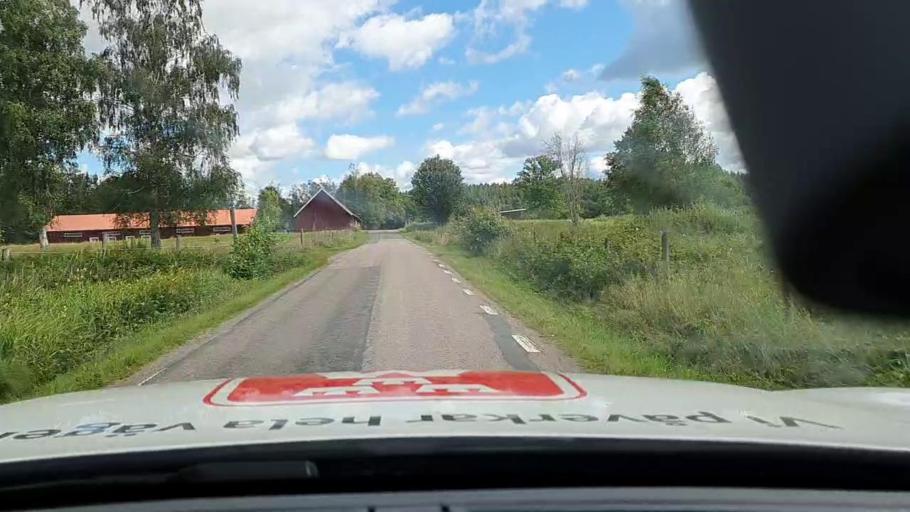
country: SE
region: Vaestra Goetaland
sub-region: Karlsborgs Kommun
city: Molltorp
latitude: 58.6038
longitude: 14.3065
